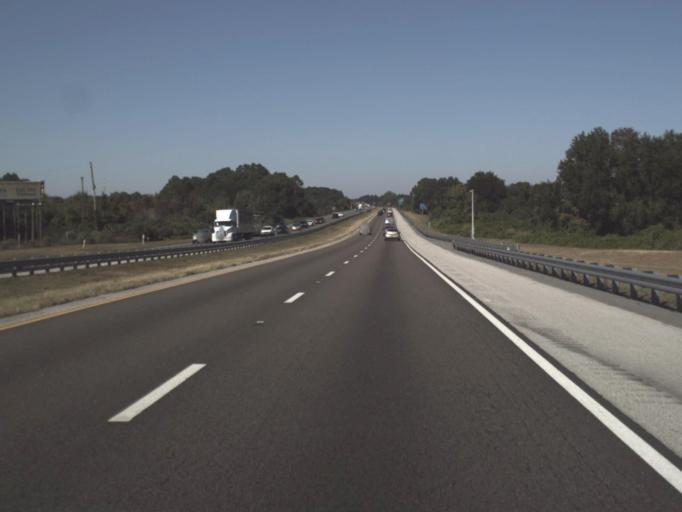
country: US
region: Florida
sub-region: Lake County
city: Minneola
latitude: 28.6386
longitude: -81.7829
